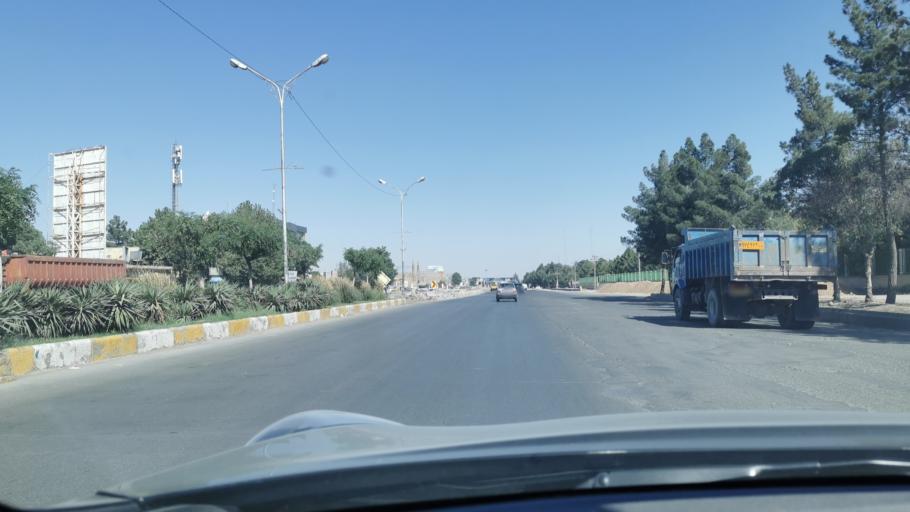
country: IR
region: Razavi Khorasan
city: Chenaran
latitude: 36.6388
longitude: 59.1218
